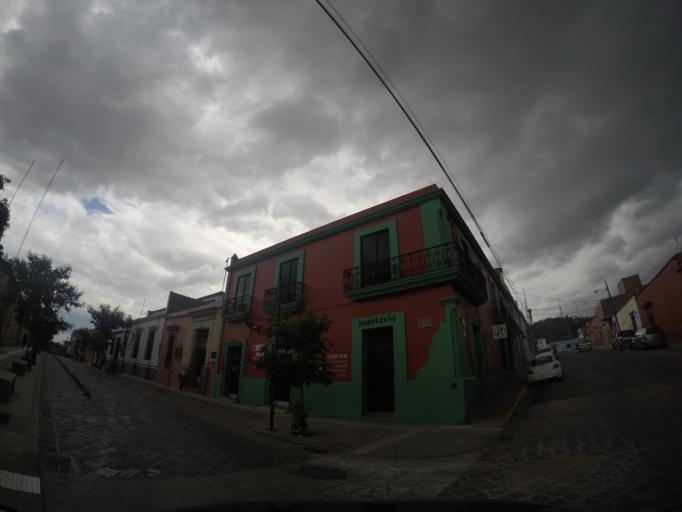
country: MX
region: Oaxaca
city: Oaxaca de Juarez
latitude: 17.0686
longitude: -96.7242
